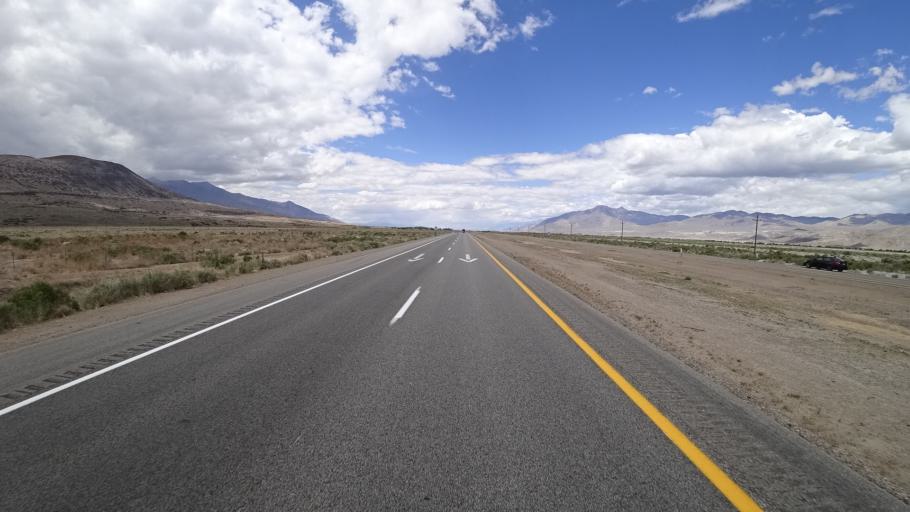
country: US
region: California
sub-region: Inyo County
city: Big Pine
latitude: 37.0971
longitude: -118.2504
